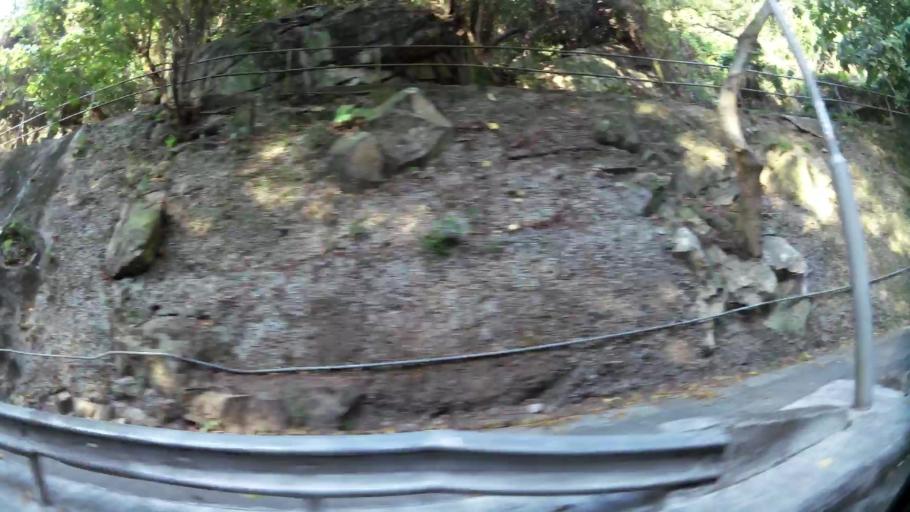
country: HK
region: Wanchai
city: Wan Chai
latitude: 22.2801
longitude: 114.1939
